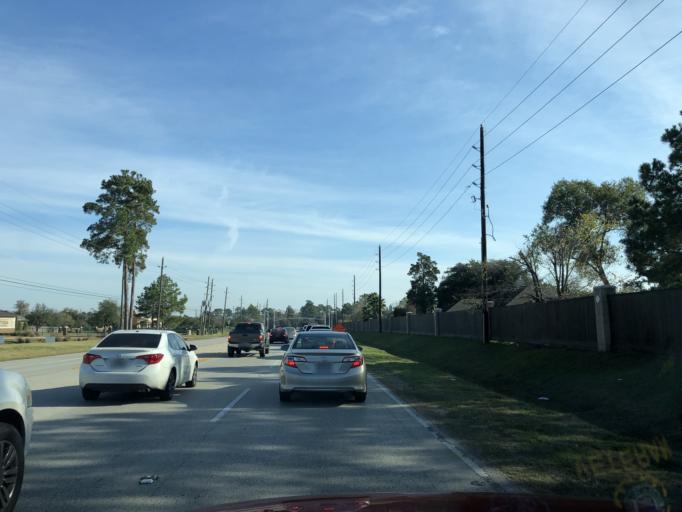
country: US
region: Texas
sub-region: Harris County
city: Tomball
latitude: 30.0367
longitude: -95.5510
